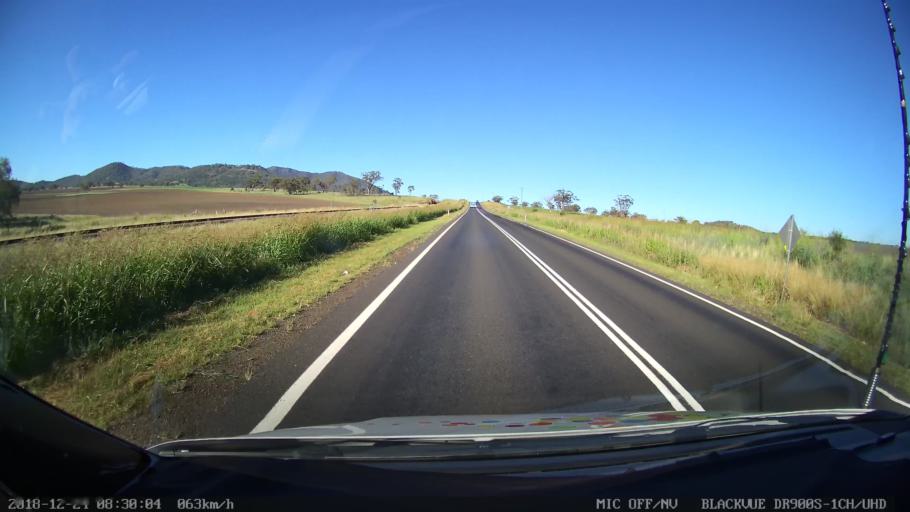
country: AU
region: New South Wales
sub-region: Tamworth Municipality
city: Phillip
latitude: -31.2658
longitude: 150.7285
